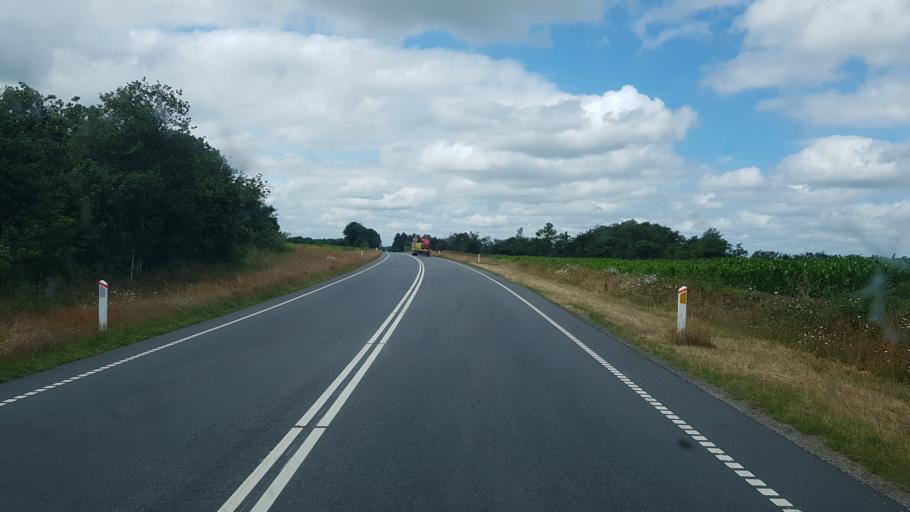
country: DK
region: South Denmark
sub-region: Vejen Kommune
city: Holsted
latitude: 55.5169
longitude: 8.8399
